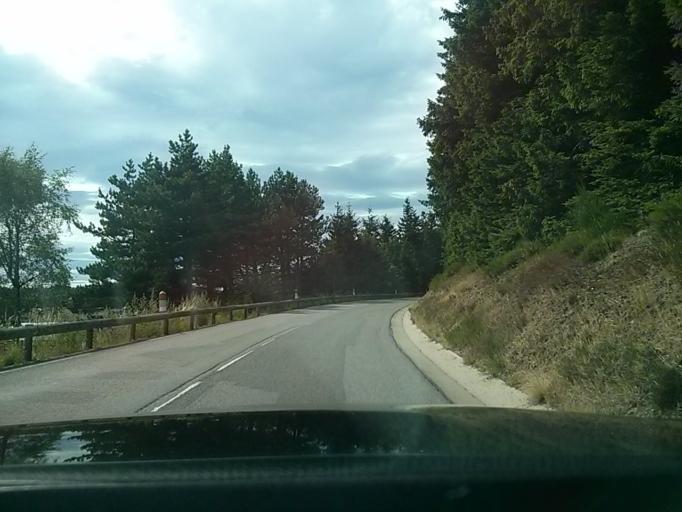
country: FR
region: Rhone-Alpes
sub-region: Departement de la Loire
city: Saint-Genest-Malifaux
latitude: 45.3711
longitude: 4.5068
